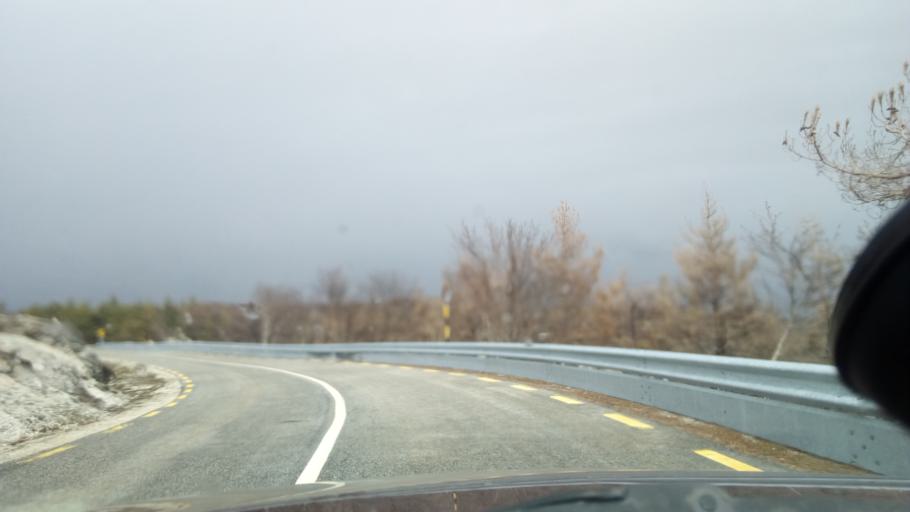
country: PT
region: Guarda
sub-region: Manteigas
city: Manteigas
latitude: 40.4218
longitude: -7.5918
